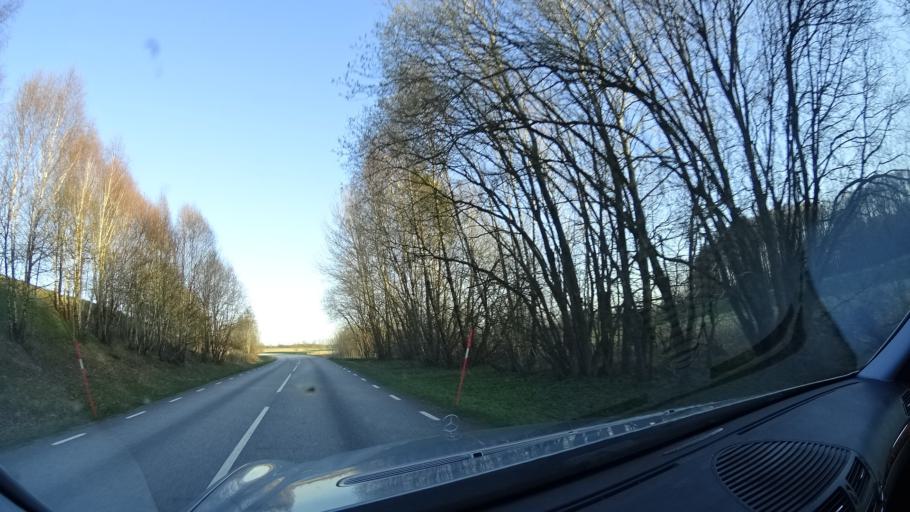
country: SE
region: Skane
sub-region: Klippans Kommun
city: Ljungbyhed
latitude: 55.9675
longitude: 13.2155
